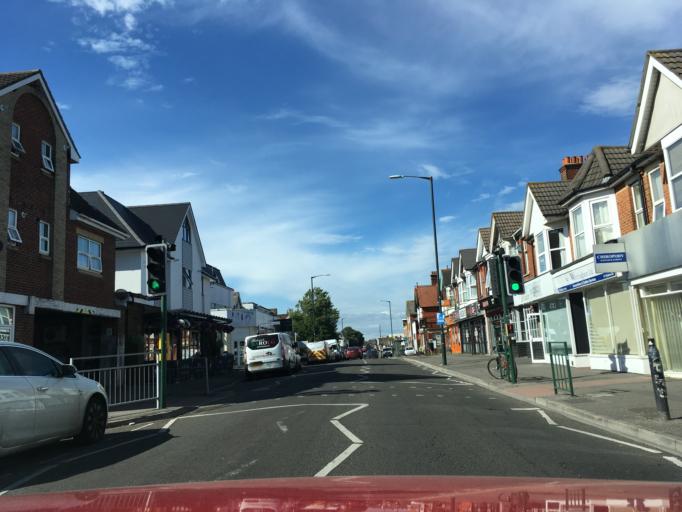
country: GB
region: England
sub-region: Bournemouth
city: Bournemouth
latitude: 50.7456
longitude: -1.8782
